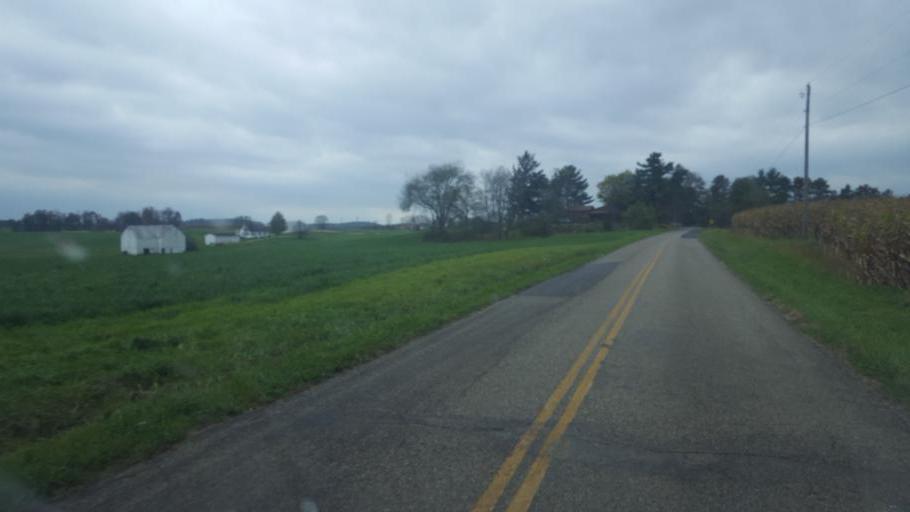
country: US
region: Ohio
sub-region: Carroll County
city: Carrollton
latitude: 40.5333
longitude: -81.1688
